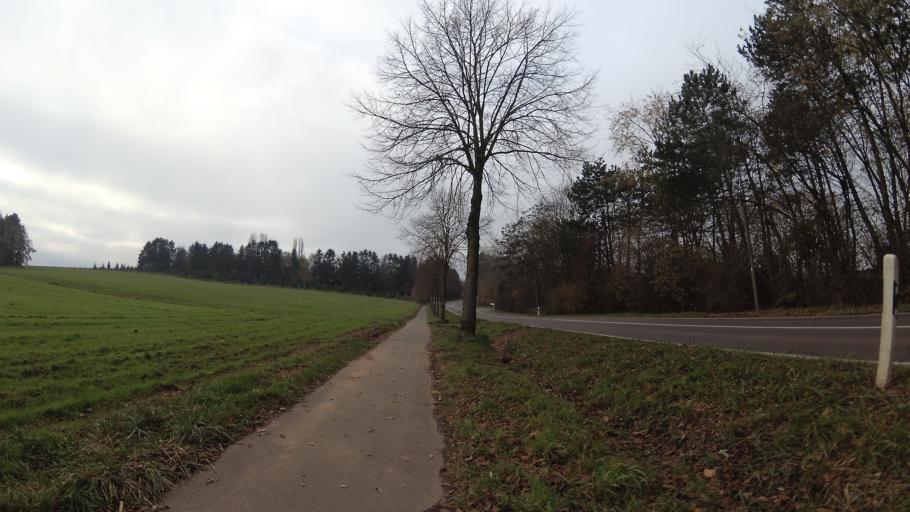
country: DE
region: Saarland
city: Illingen
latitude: 49.3624
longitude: 7.0309
